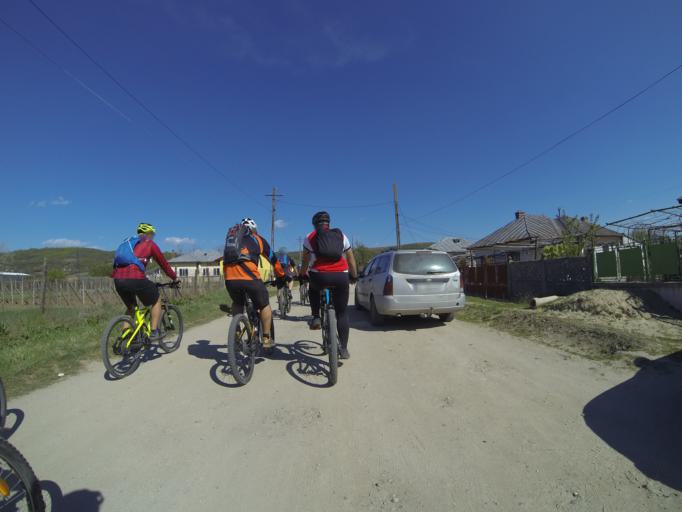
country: RO
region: Dolj
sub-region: Comuna Goesti
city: Goesti
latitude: 44.4988
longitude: 23.7537
